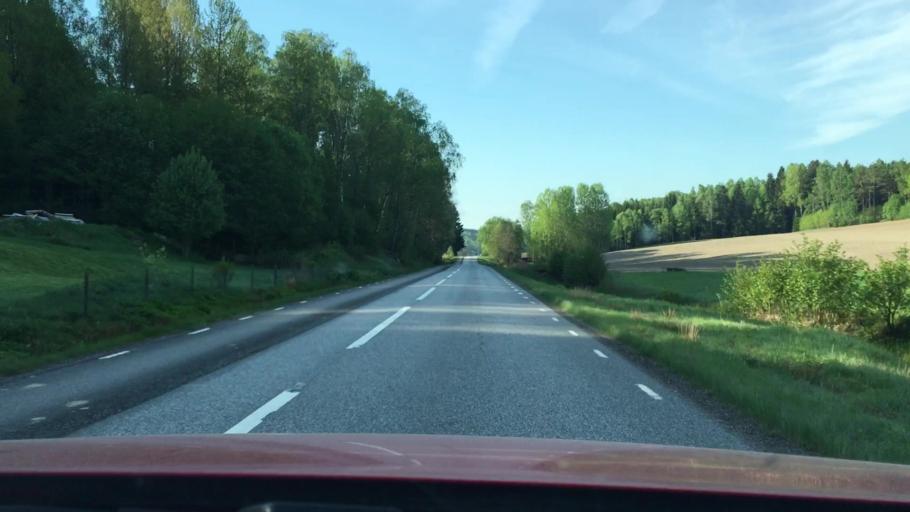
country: SE
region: Vaestra Goetaland
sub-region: Munkedals Kommun
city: Munkedal
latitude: 58.6173
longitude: 11.5585
